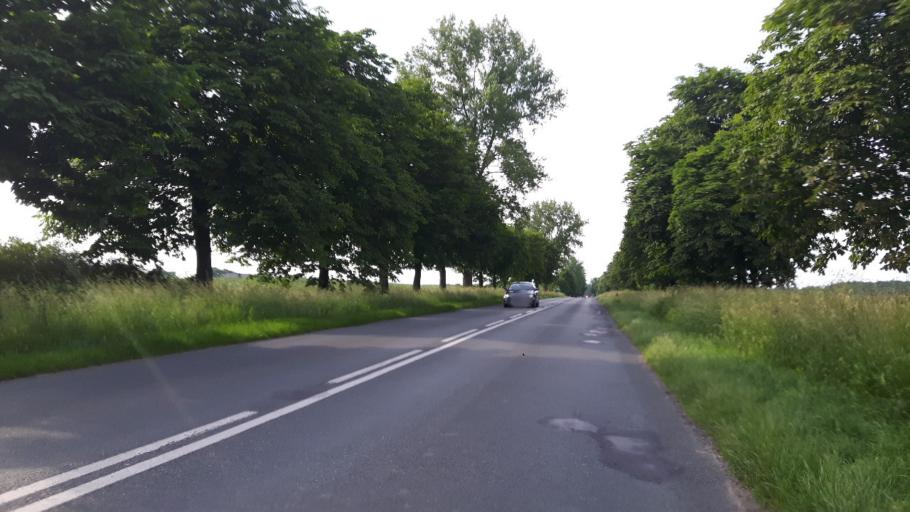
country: PL
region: West Pomeranian Voivodeship
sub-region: Powiat gryficki
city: Gryfice
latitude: 53.8973
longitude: 15.2050
